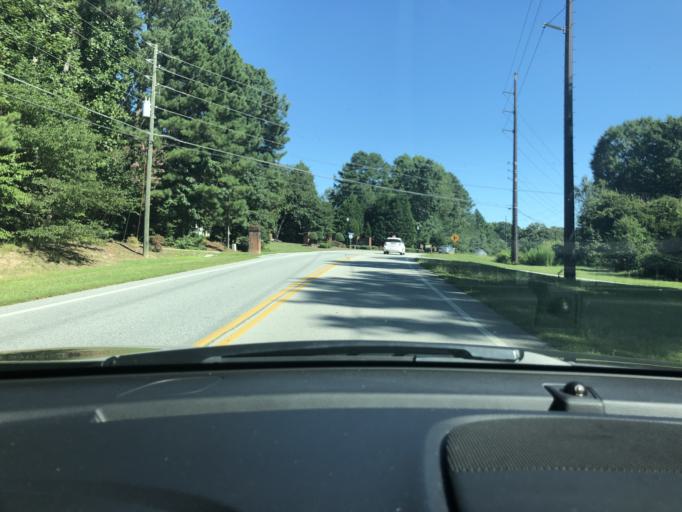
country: US
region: Georgia
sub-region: Gwinnett County
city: Grayson
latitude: 33.9229
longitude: -83.9483
